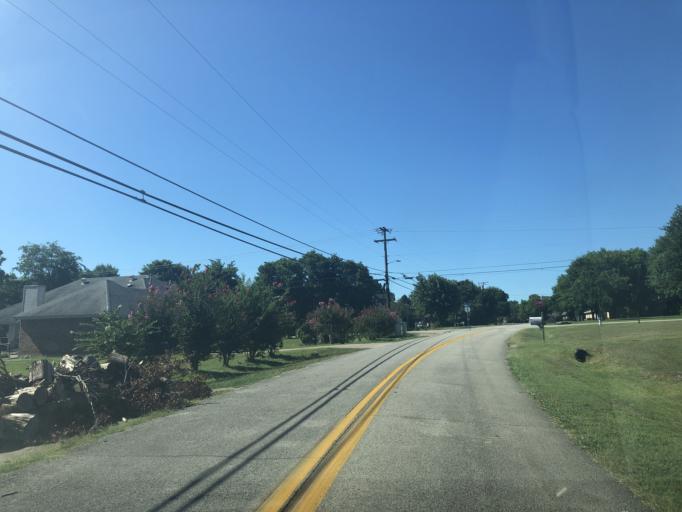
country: US
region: Texas
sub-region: Dallas County
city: Duncanville
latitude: 32.6568
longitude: -96.9354
